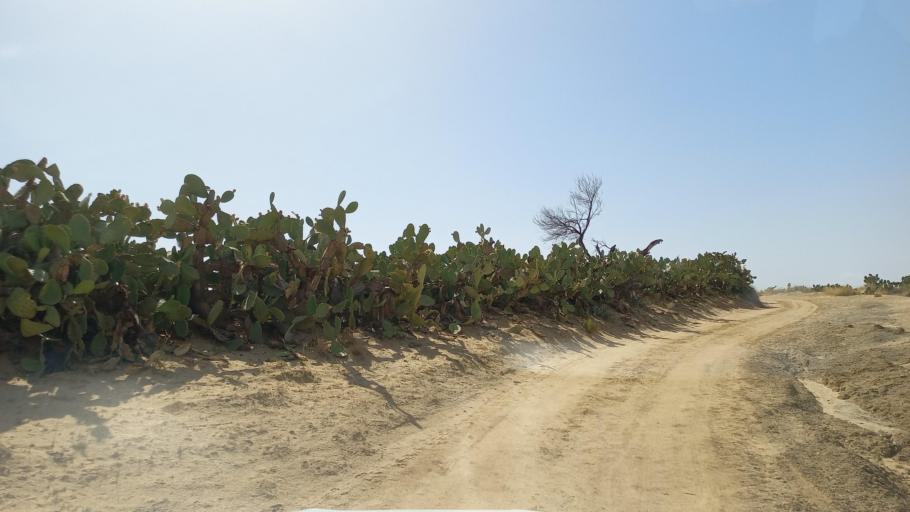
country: TN
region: Al Qasrayn
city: Kasserine
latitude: 35.2000
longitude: 9.0347
